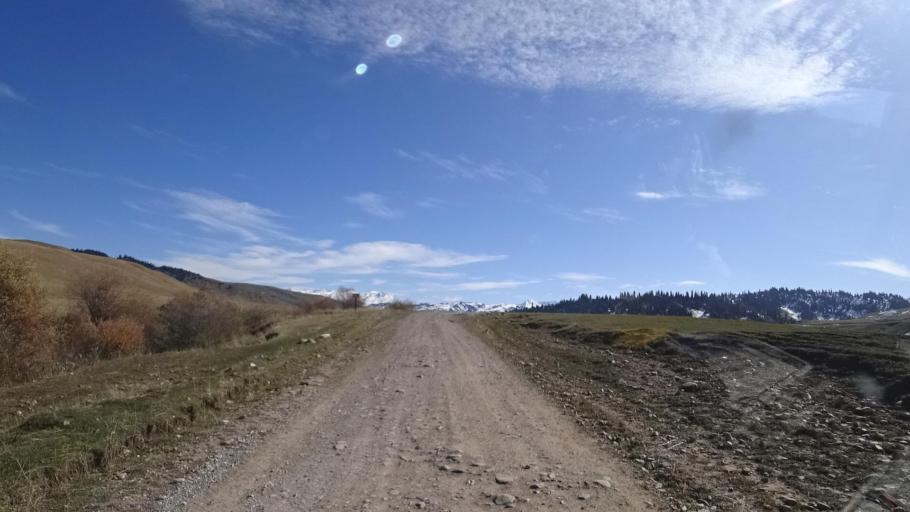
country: KZ
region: Almaty Oblysy
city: Kegen
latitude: 42.7363
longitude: 79.0161
